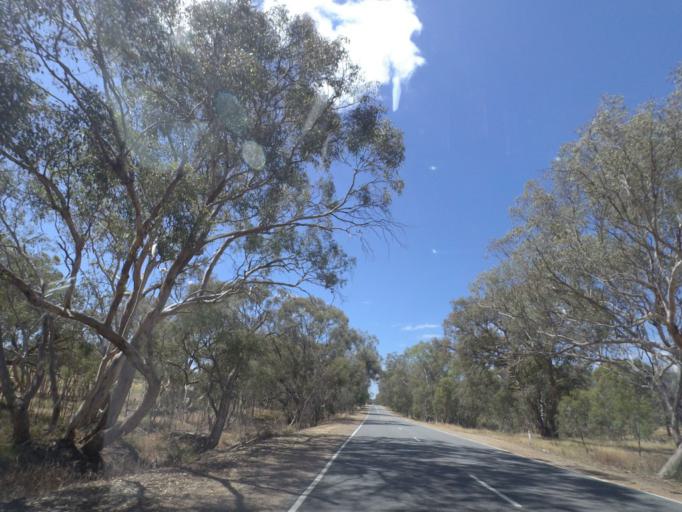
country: AU
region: Victoria
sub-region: Wangaratta
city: Wangaratta
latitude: -36.4465
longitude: 146.2414
